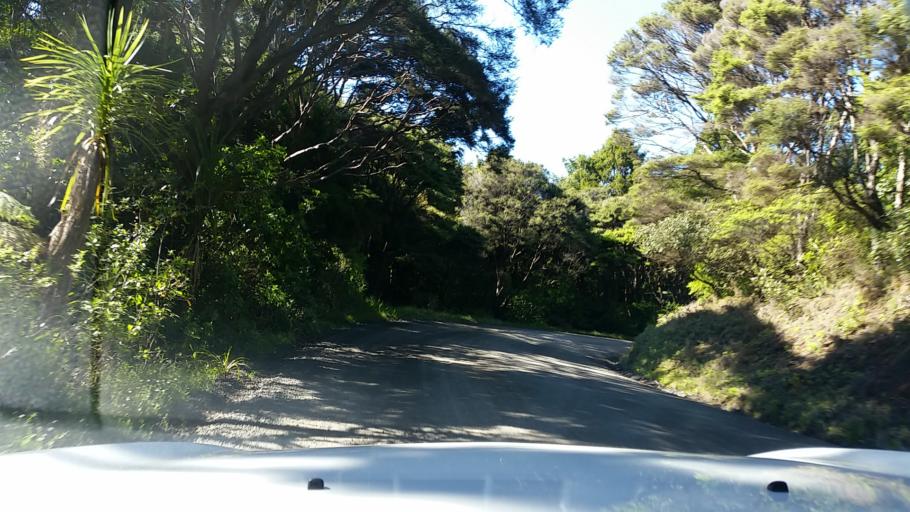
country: NZ
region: Auckland
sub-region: Auckland
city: Titirangi
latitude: -37.0222
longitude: 174.5377
